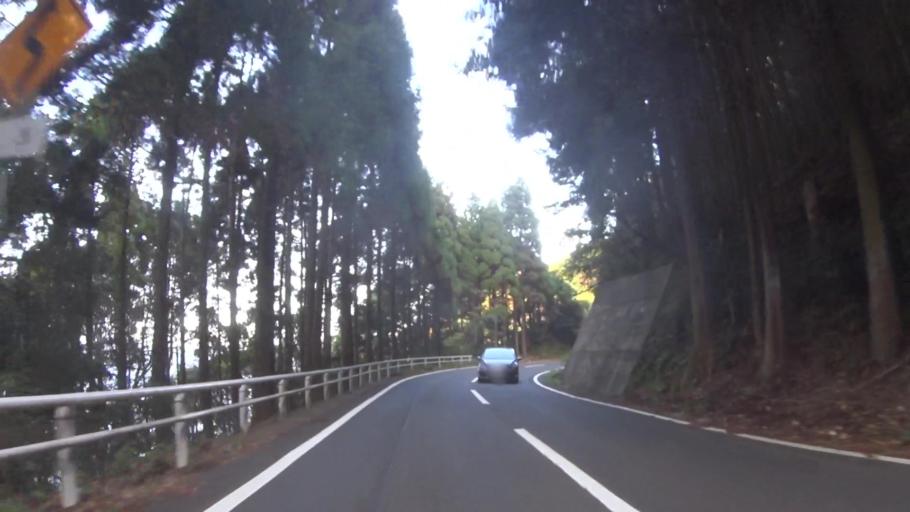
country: JP
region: Kyoto
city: Miyazu
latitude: 35.7561
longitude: 135.2475
